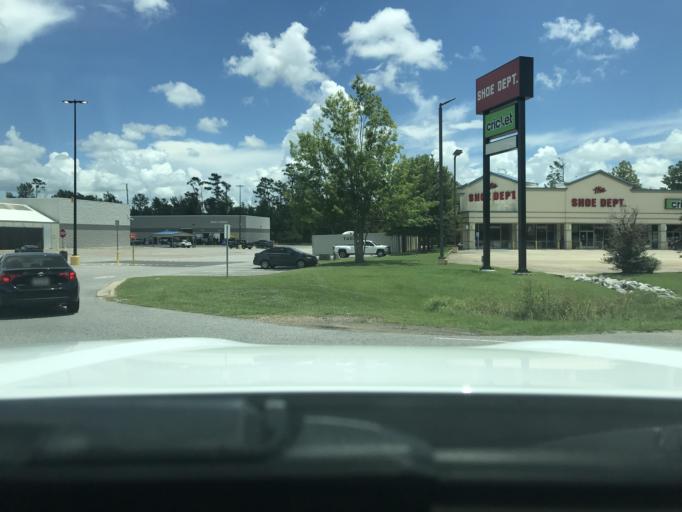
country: US
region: Louisiana
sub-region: Calcasieu Parish
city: Moss Bluff
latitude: 30.2678
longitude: -93.1813
